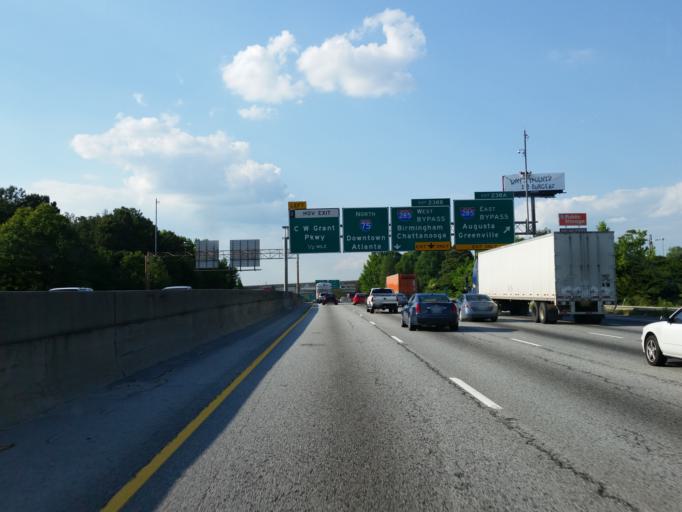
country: US
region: Georgia
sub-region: Clayton County
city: Forest Park
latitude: 33.6285
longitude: -84.4004
